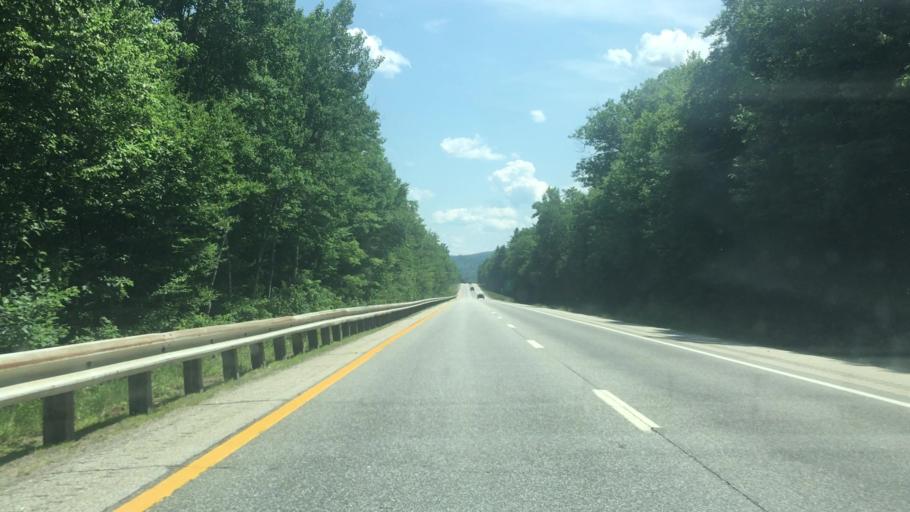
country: US
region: New Hampshire
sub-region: Merrimack County
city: Sutton
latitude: 43.3079
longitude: -71.8448
